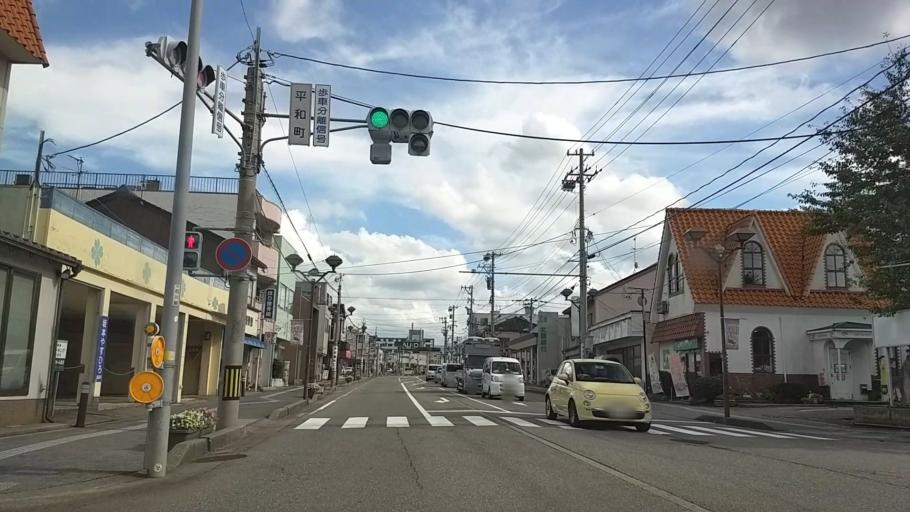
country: JP
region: Ishikawa
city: Nonoichi
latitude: 36.5427
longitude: 136.6628
